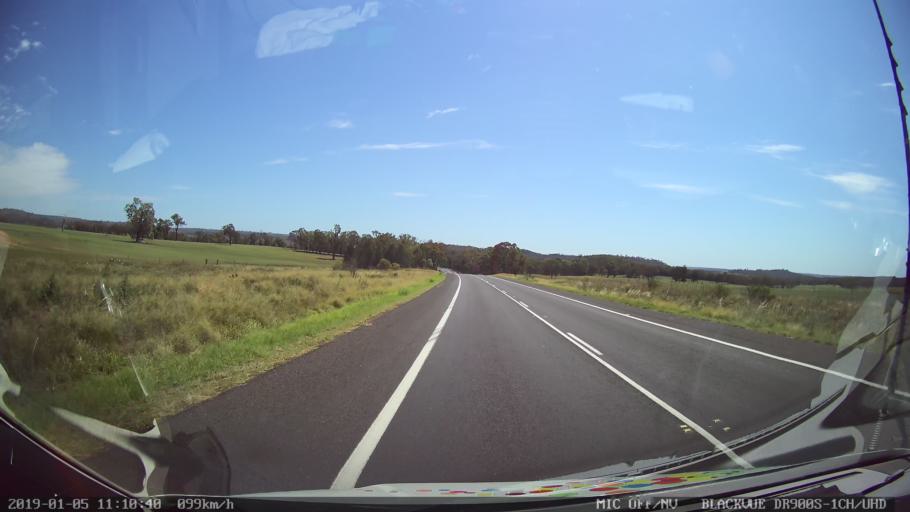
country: AU
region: New South Wales
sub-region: Warrumbungle Shire
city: Coonabarabran
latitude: -31.4038
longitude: 149.2466
